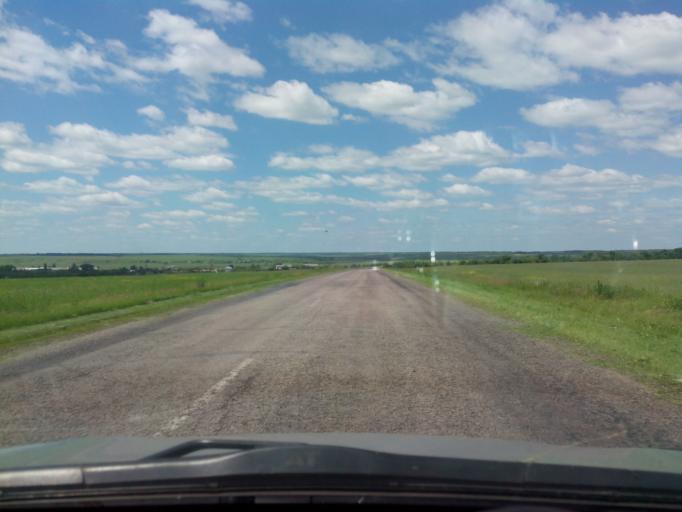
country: RU
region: Voronezj
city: Ternovka
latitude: 51.5924
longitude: 41.8069
